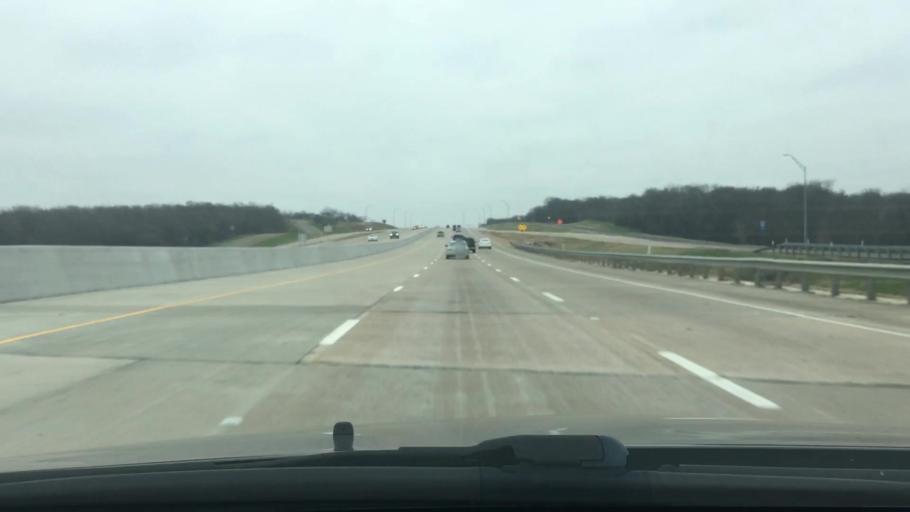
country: US
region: Texas
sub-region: Freestone County
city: Wortham
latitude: 31.9092
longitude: -96.3912
